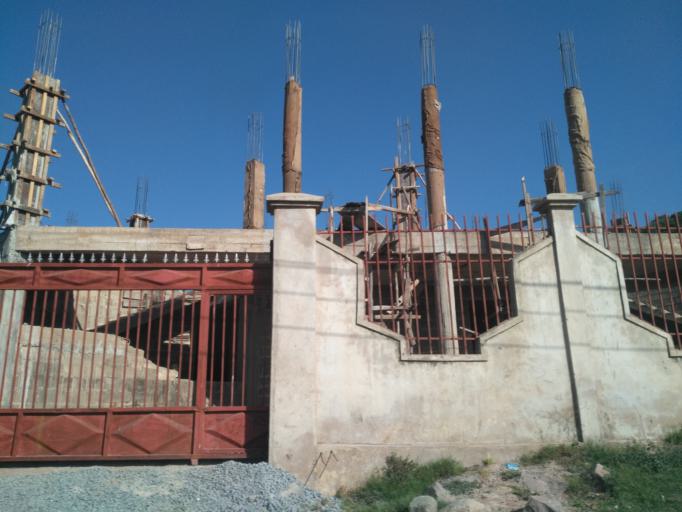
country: TZ
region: Mwanza
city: Mwanza
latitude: -2.5002
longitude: 32.8944
